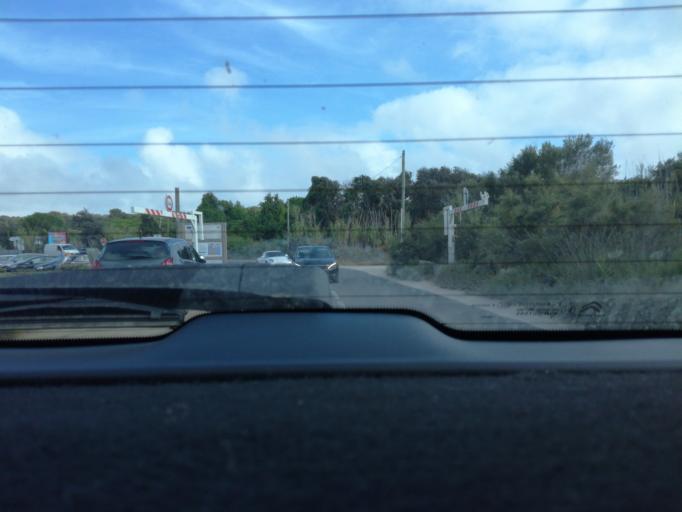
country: FR
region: Provence-Alpes-Cote d'Azur
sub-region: Departement du Var
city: Hyeres
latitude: 43.0451
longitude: 6.1344
